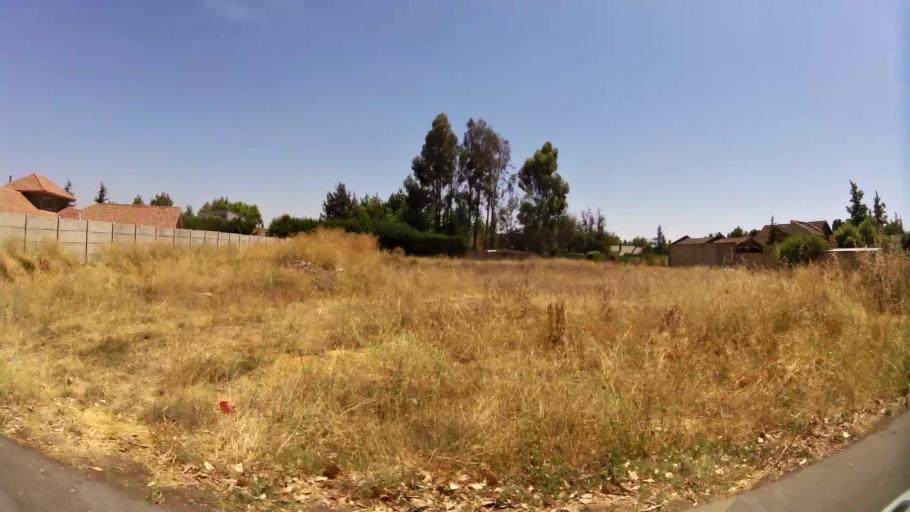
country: CL
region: Maule
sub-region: Provincia de Curico
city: Curico
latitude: -34.9964
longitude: -71.2069
